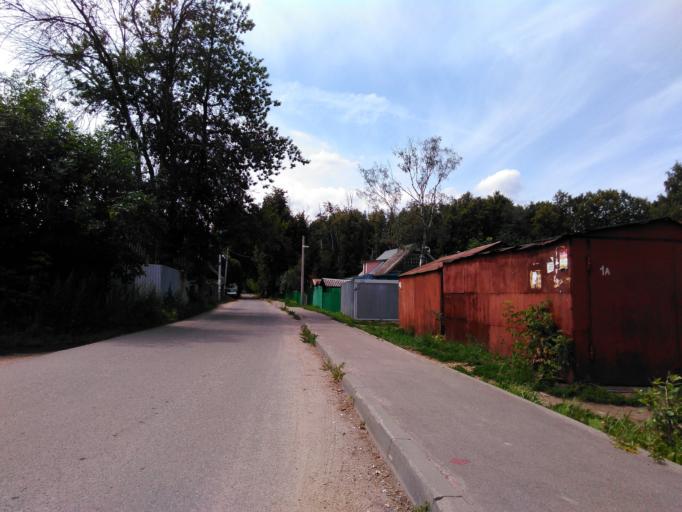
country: RU
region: Moskovskaya
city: Pravdinskiy
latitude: 56.0606
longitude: 37.8508
